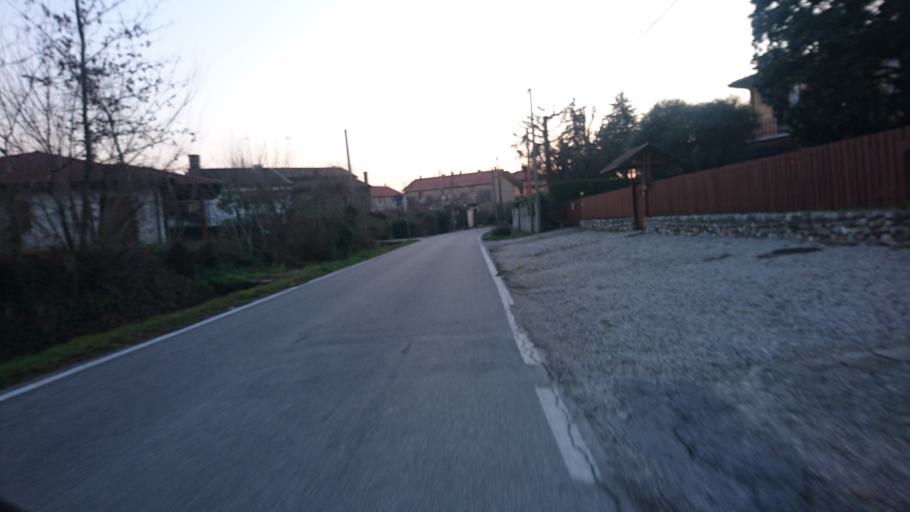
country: IT
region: Veneto
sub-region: Provincia di Padova
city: Legnaro
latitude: 45.3577
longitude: 11.9630
